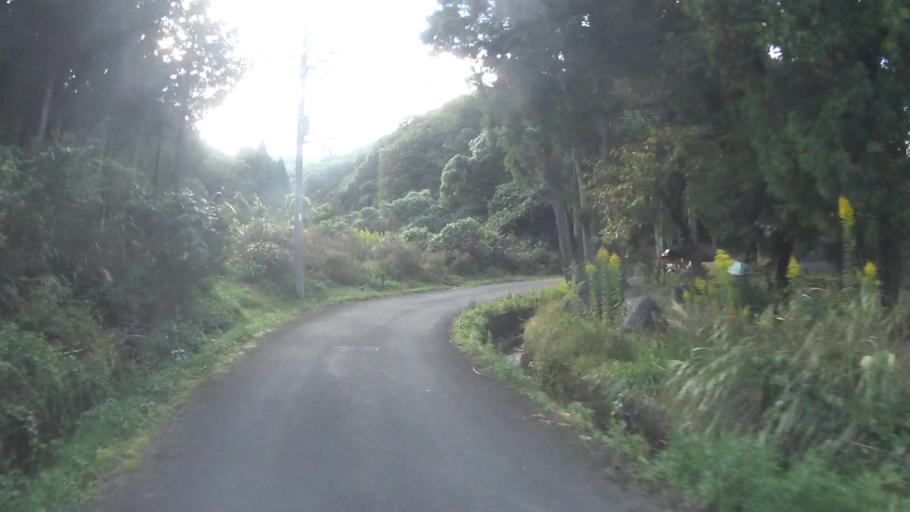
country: JP
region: Kyoto
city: Maizuru
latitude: 35.5660
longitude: 135.4231
